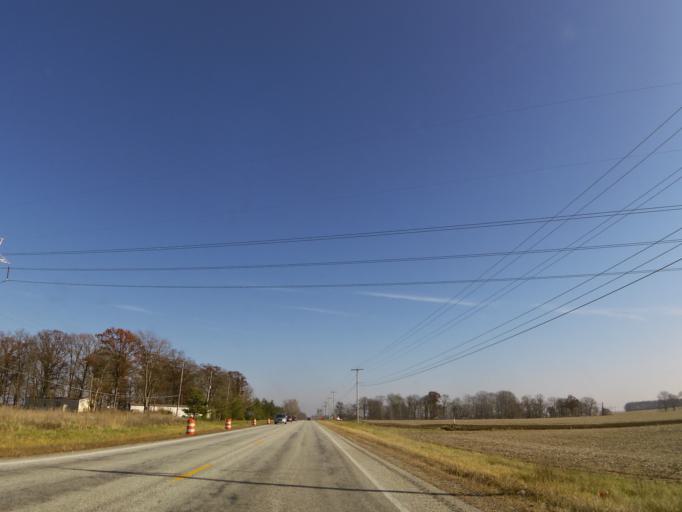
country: US
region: Indiana
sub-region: Shelby County
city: Shelbyville
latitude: 39.5306
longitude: -85.7261
